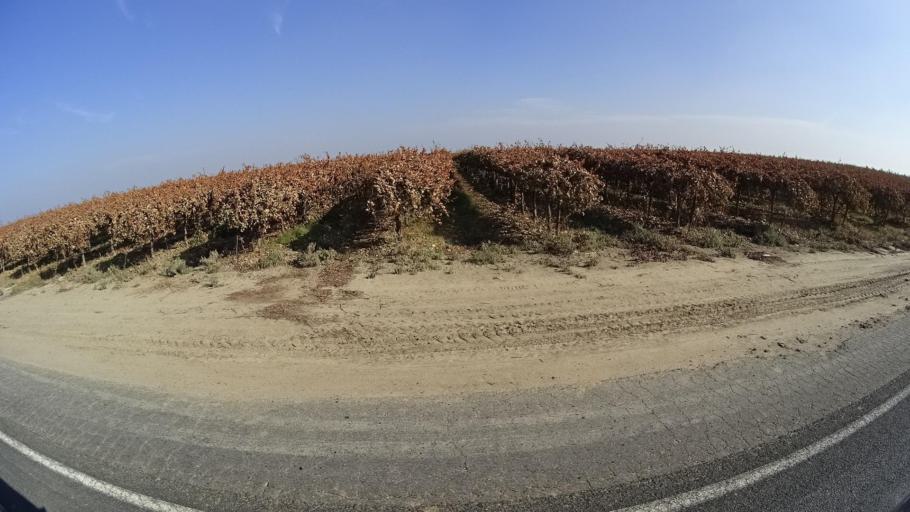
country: US
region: California
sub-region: Kern County
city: McFarland
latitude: 35.6469
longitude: -119.1956
